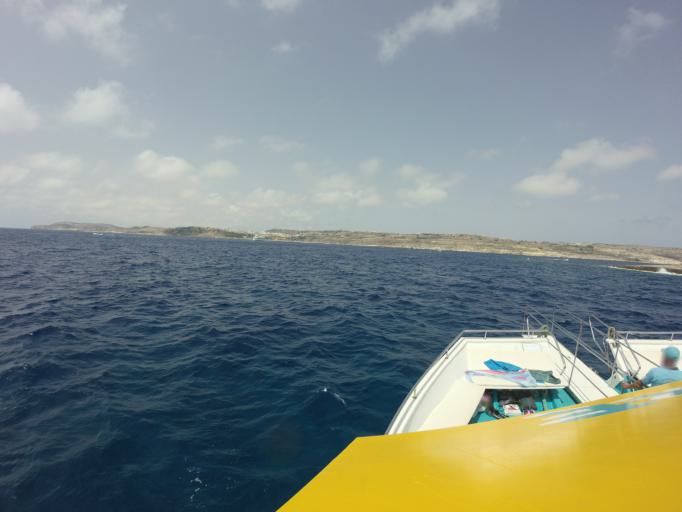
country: MT
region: Il-Qala
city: Qala
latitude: 36.0125
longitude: 14.3167
